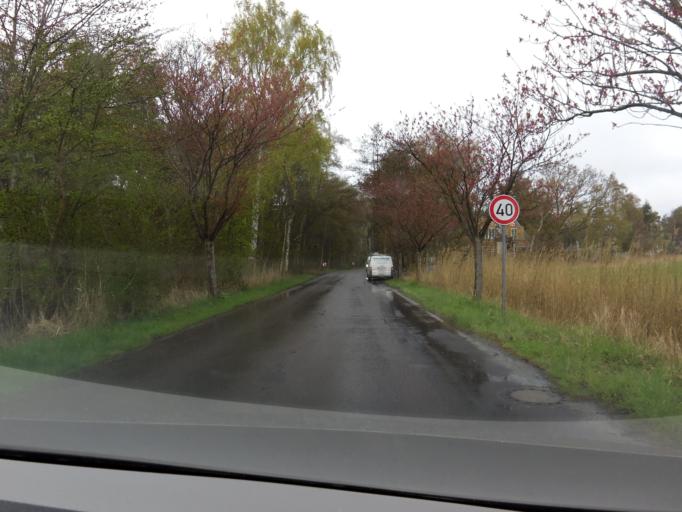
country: DE
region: Mecklenburg-Vorpommern
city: Zingst
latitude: 54.4373
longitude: 12.7246
